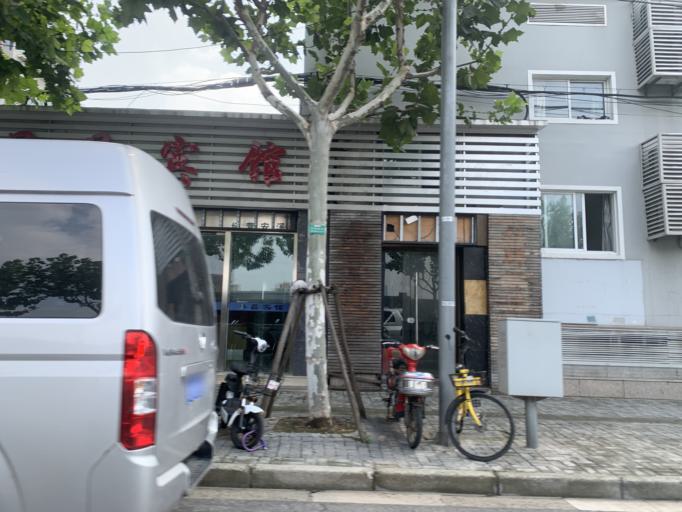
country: CN
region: Shanghai Shi
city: Luwan
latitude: 31.1826
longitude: 121.4928
